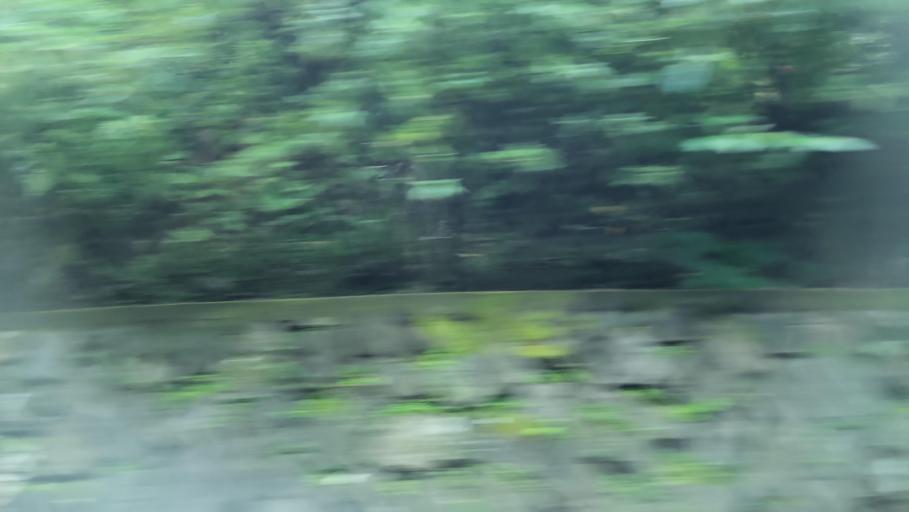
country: TW
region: Taipei
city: Taipei
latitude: 25.1442
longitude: 121.6081
